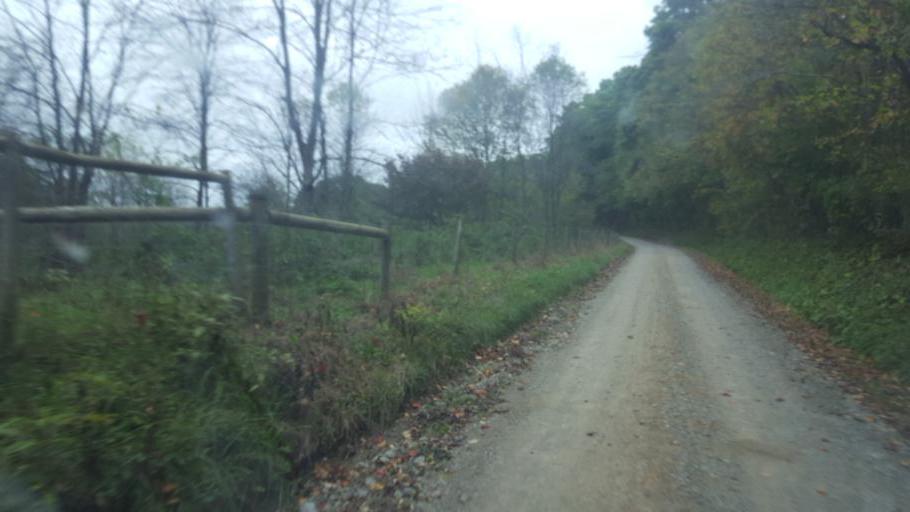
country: US
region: Ohio
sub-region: Harrison County
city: Cadiz
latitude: 40.3875
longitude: -81.0442
